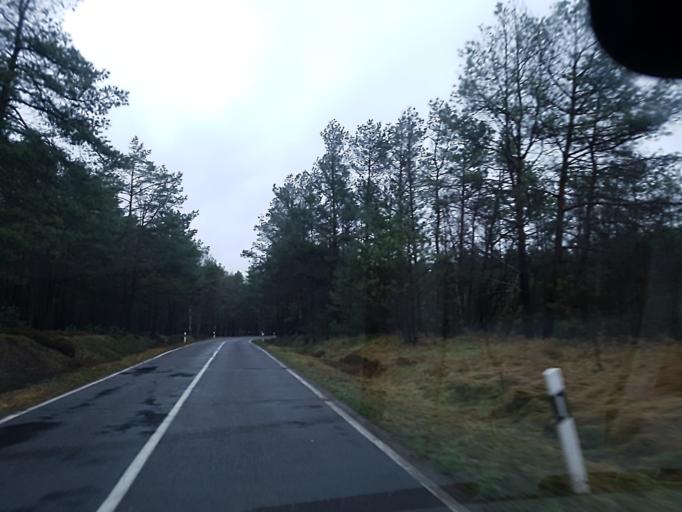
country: DE
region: Brandenburg
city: Schonewalde
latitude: 51.6231
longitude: 13.6391
